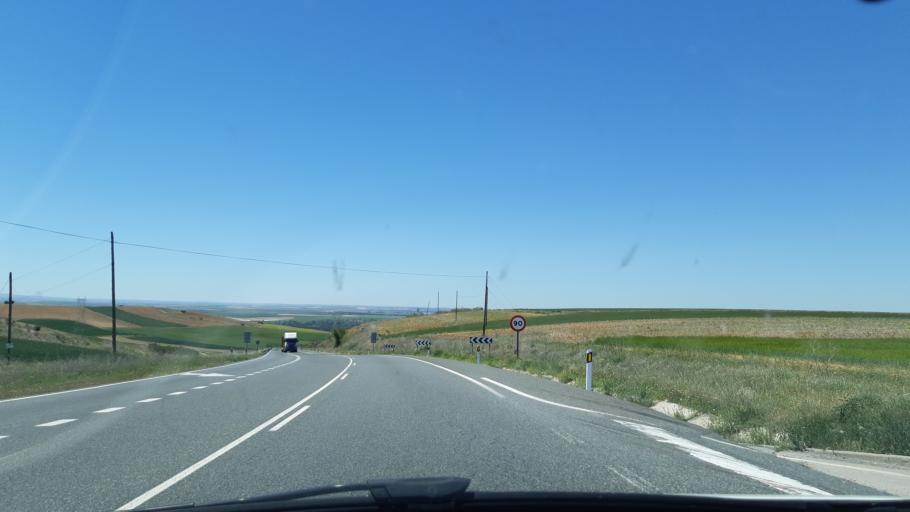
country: ES
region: Castille and Leon
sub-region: Provincia de Segovia
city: Labajos
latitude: 40.8434
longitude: -4.5252
